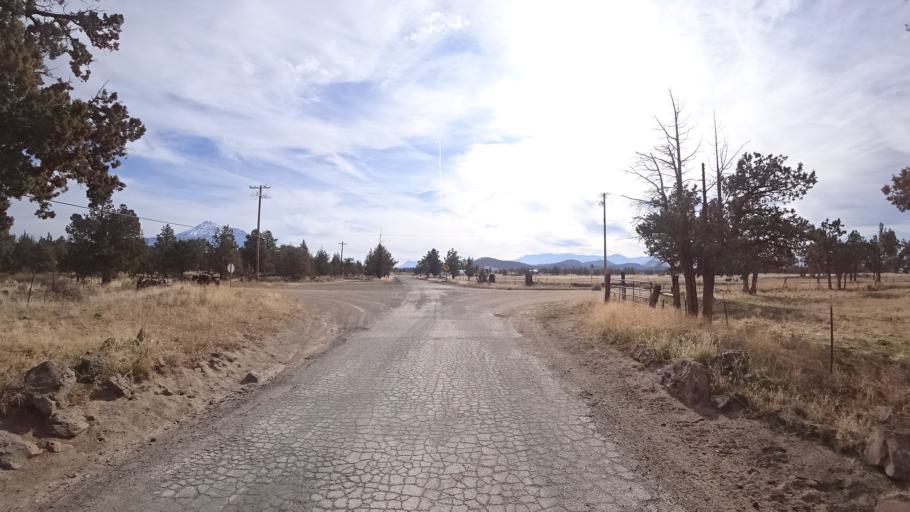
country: US
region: California
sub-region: Siskiyou County
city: Weed
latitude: 41.5958
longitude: -122.4033
